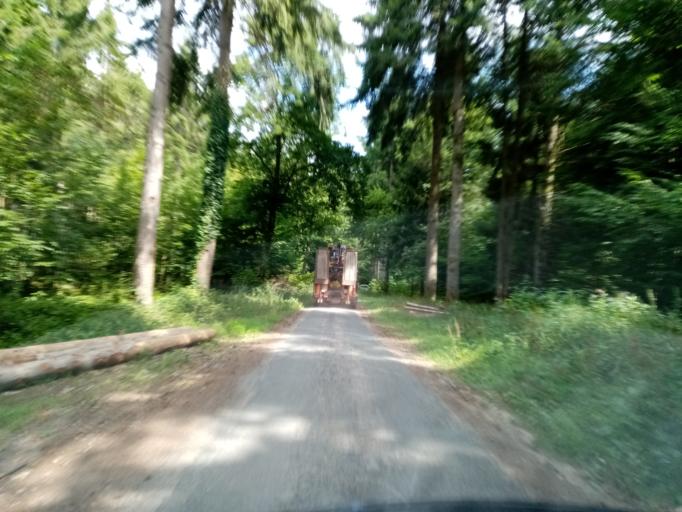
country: FR
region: Alsace
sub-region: Departement du Bas-Rhin
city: Dambach-la-Ville
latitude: 48.3451
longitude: 7.3907
